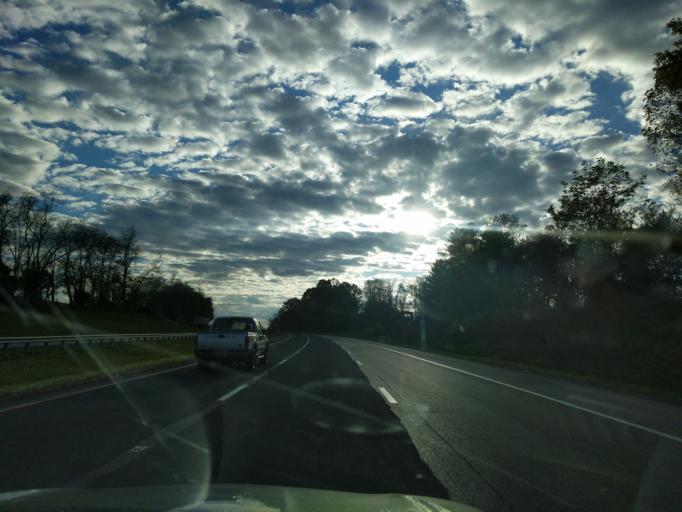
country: US
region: Virginia
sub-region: Washington County
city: Emory
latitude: 36.7374
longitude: -81.9003
